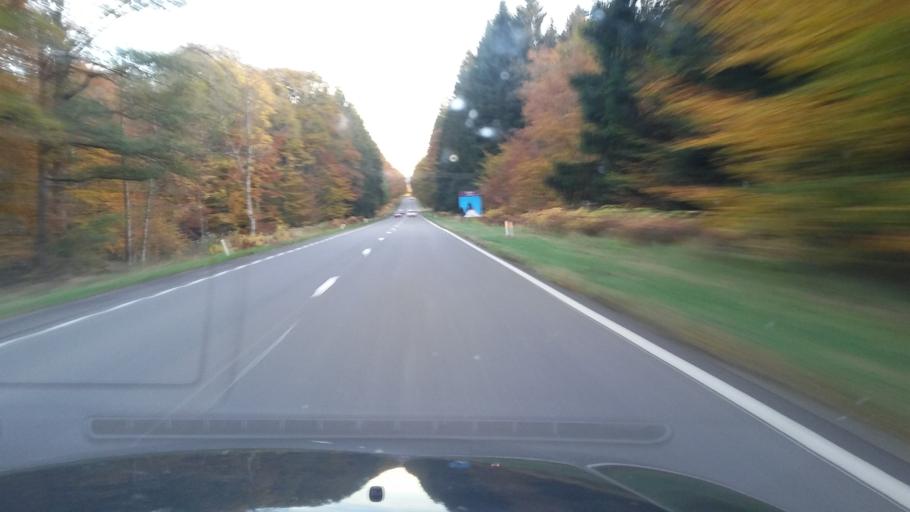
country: BE
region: Wallonia
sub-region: Province du Luxembourg
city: Herbeumont
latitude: 49.7461
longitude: 5.2142
